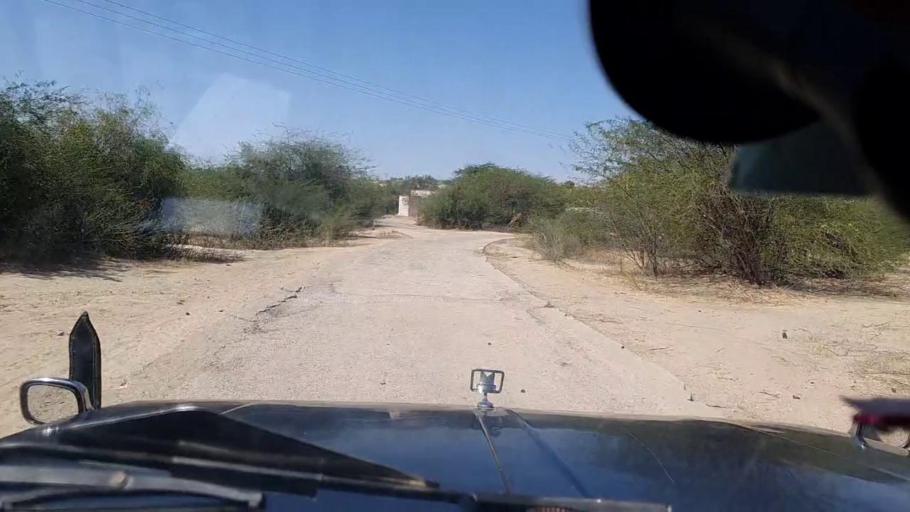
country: PK
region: Sindh
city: Mithi
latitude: 24.5936
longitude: 69.7112
